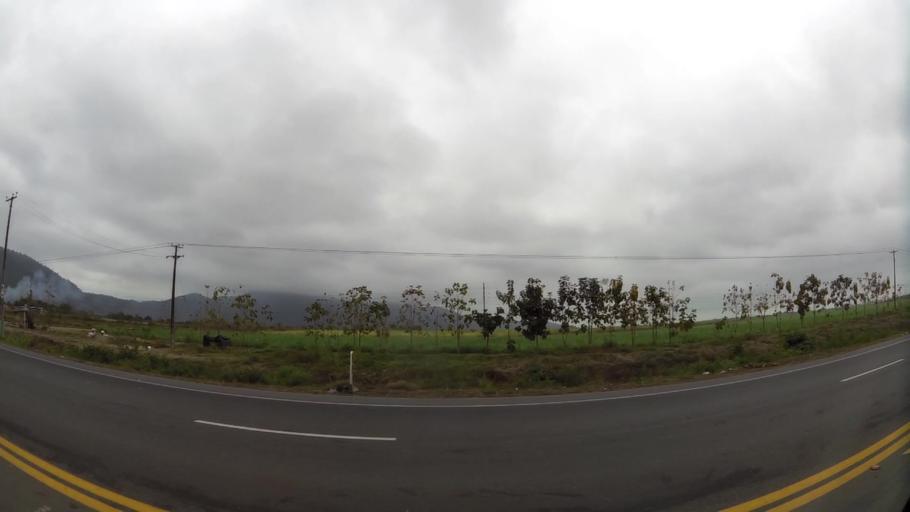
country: EC
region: Guayas
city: Naranjal
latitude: -2.4763
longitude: -79.6193
